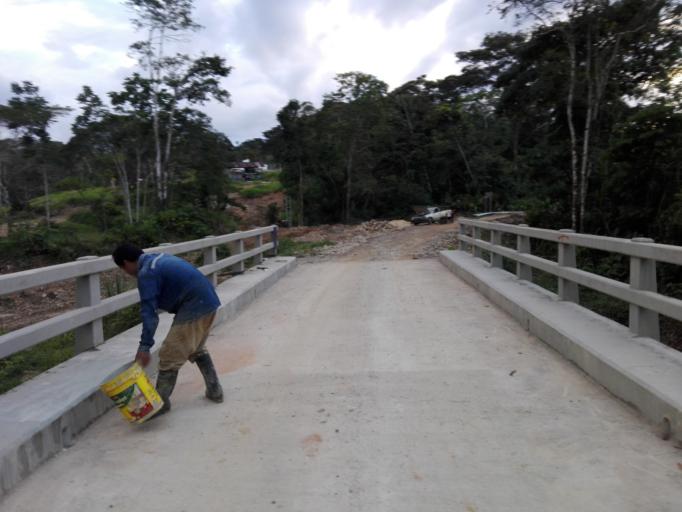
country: BO
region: Cochabamba
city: Chimore
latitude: -17.0566
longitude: -65.0934
